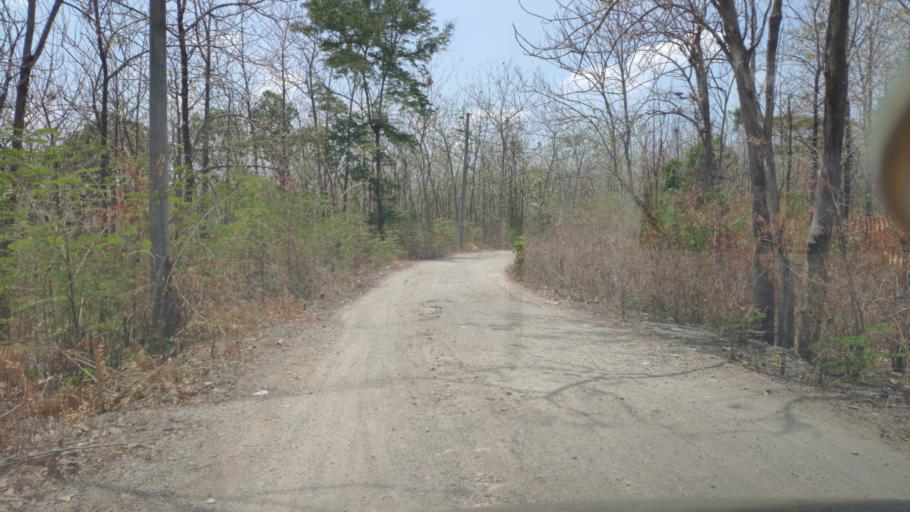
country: ID
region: Central Java
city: Randublatung
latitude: -7.2634
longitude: 111.3791
